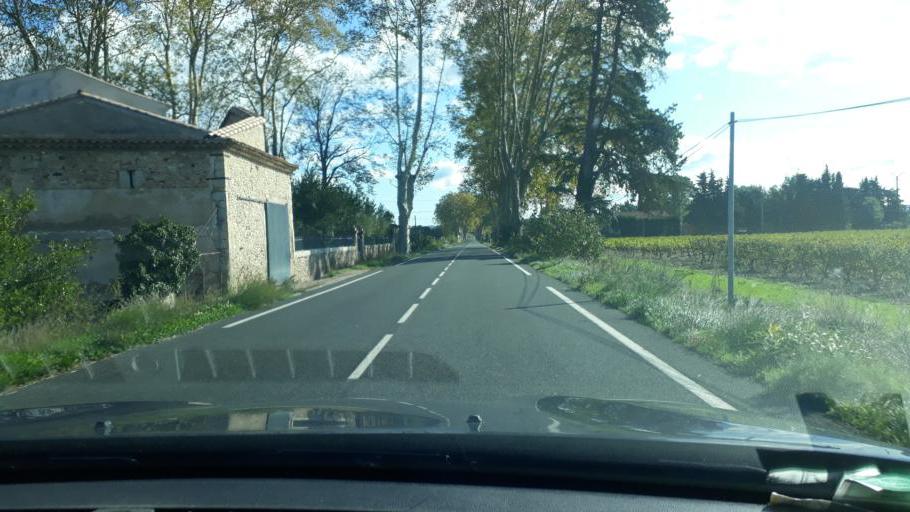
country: FR
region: Languedoc-Roussillon
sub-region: Departement de l'Herault
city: Saint-Andre-de-Sangonis
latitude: 43.6549
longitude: 3.4841
